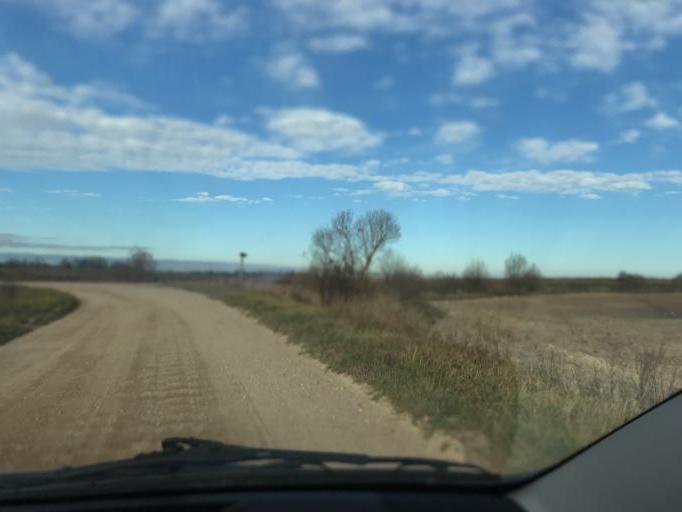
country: BY
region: Vitebsk
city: Haradok
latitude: 55.4540
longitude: 30.0337
